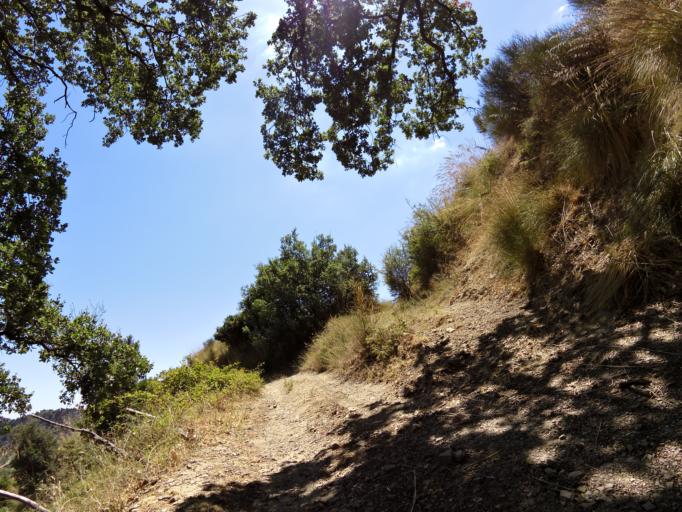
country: IT
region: Calabria
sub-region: Provincia di Reggio Calabria
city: Stilo
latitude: 38.4612
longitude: 16.4622
